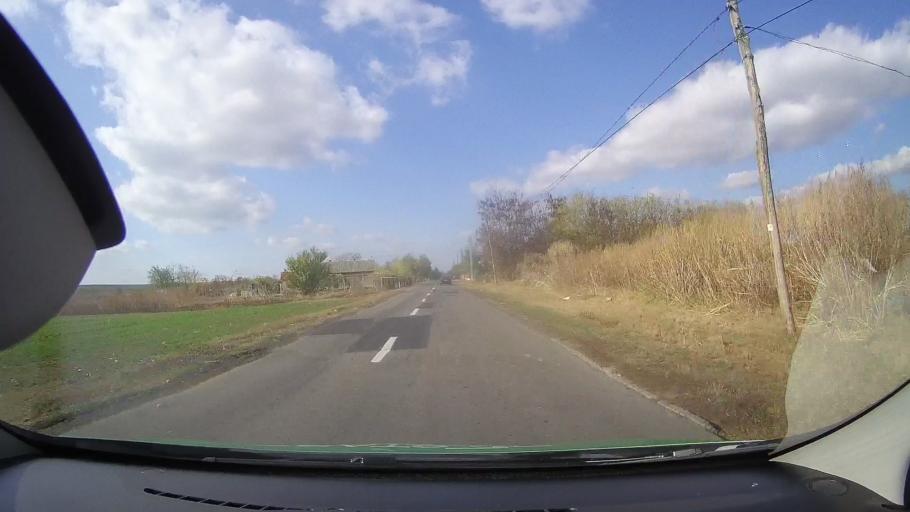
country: RO
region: Constanta
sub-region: Comuna Istria
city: Nuntasi
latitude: 44.5357
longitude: 28.6594
